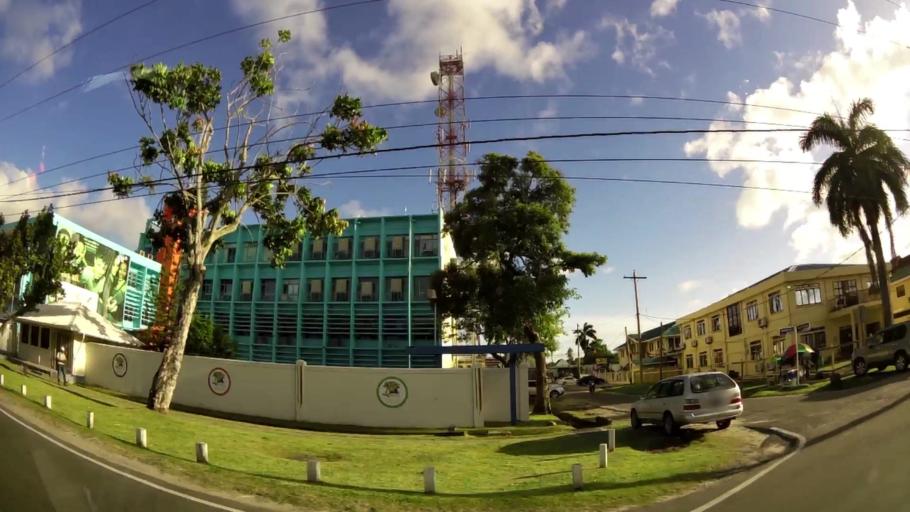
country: GY
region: Demerara-Mahaica
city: Georgetown
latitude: 6.8057
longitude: -58.1537
